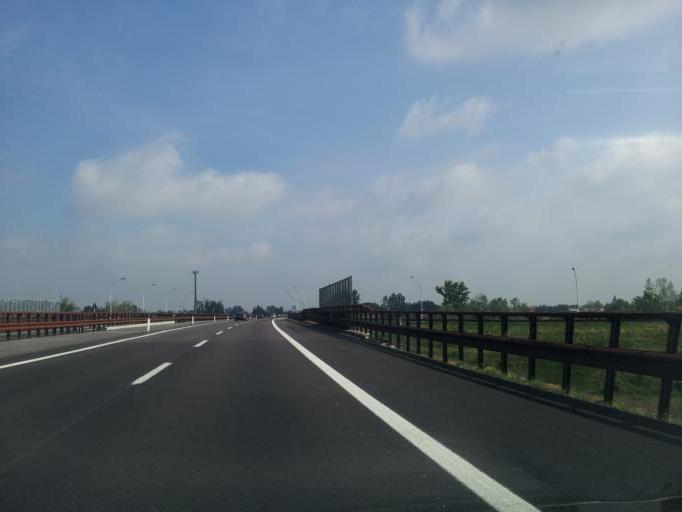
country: IT
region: Emilia-Romagna
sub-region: Provincia di Reggio Emilia
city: Rolo
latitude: 44.9101
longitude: 10.8490
